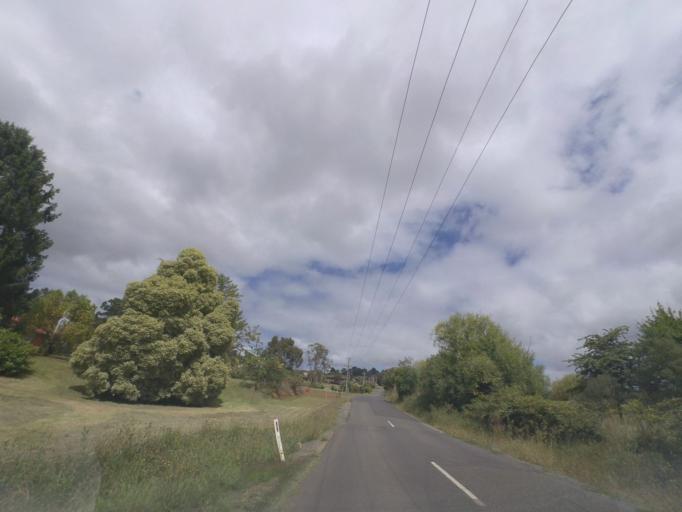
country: AU
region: Victoria
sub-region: Yarra Ranges
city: Mount Evelyn
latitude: -37.7939
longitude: 145.4470
